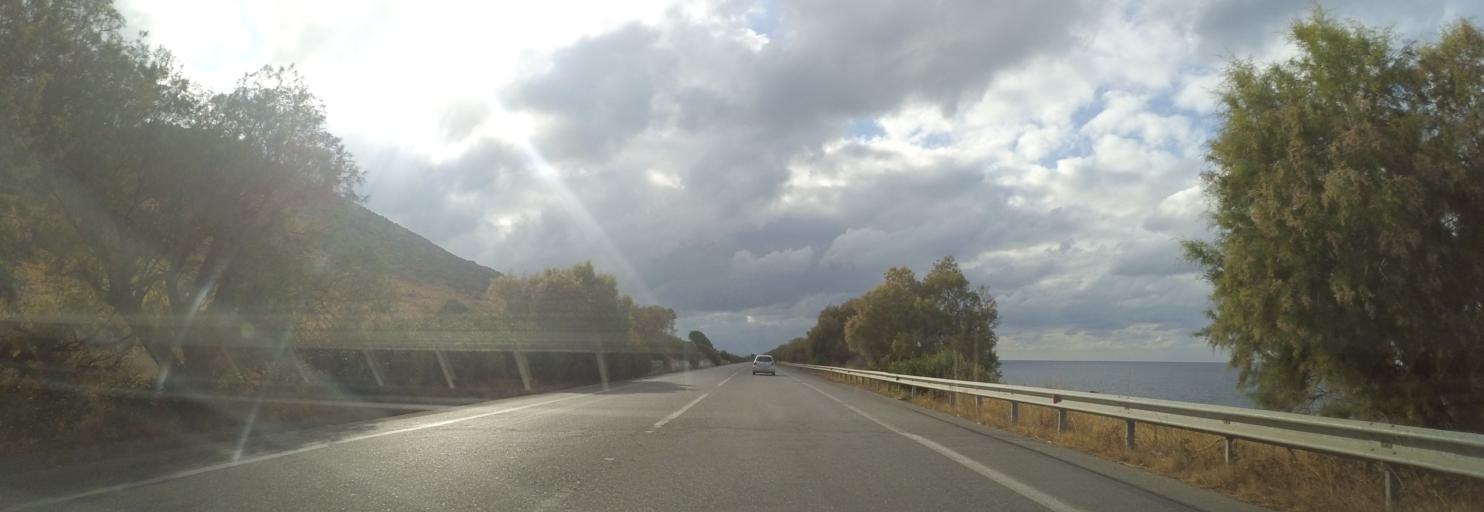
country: GR
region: Crete
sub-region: Nomos Rethymnis
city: Panormos
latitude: 35.4179
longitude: 24.6702
